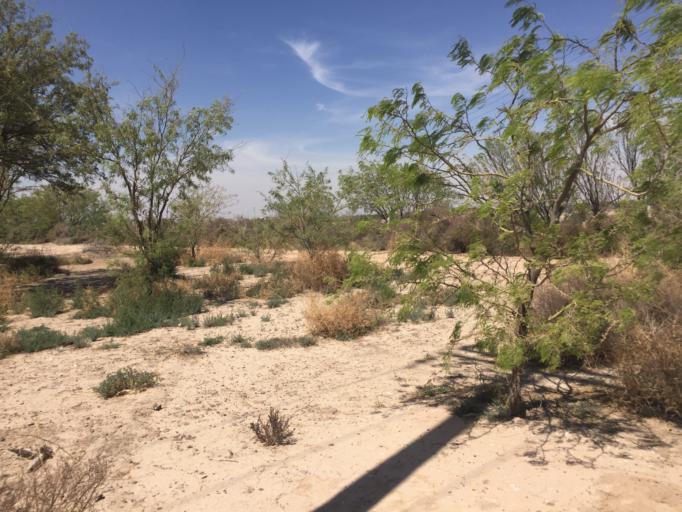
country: MX
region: Durango
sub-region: Gomez Palacio
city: Seis de Octubre
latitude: 25.7395
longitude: -103.5055
